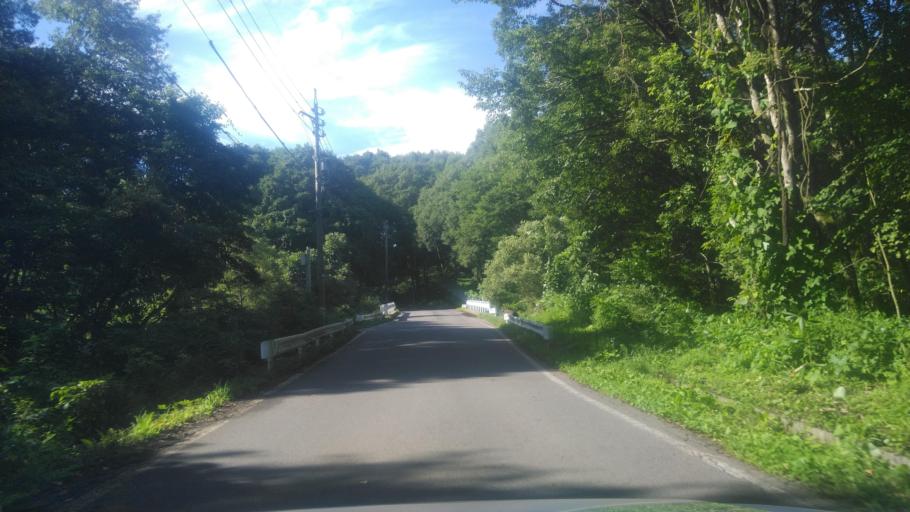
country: JP
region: Nagano
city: Nagano-shi
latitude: 36.7879
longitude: 138.1779
